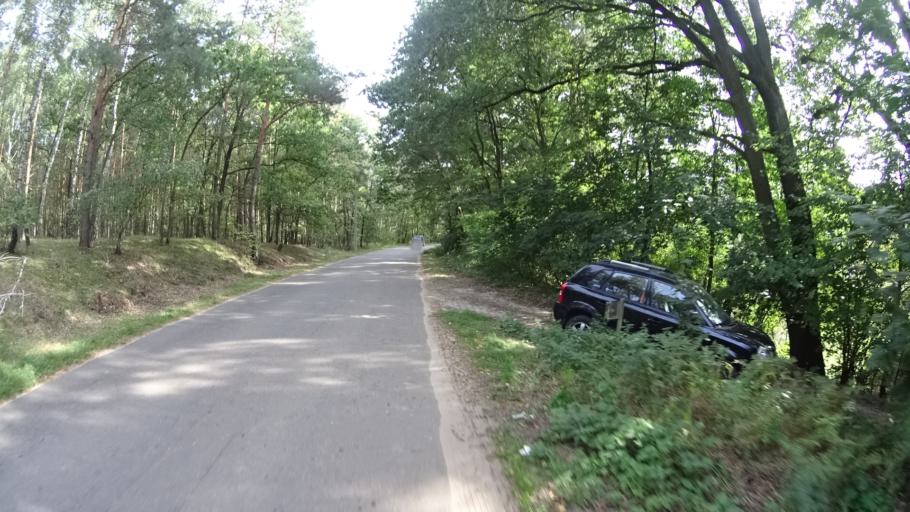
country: PL
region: Masovian Voivodeship
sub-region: Powiat legionowski
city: Serock
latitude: 52.4950
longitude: 21.0847
